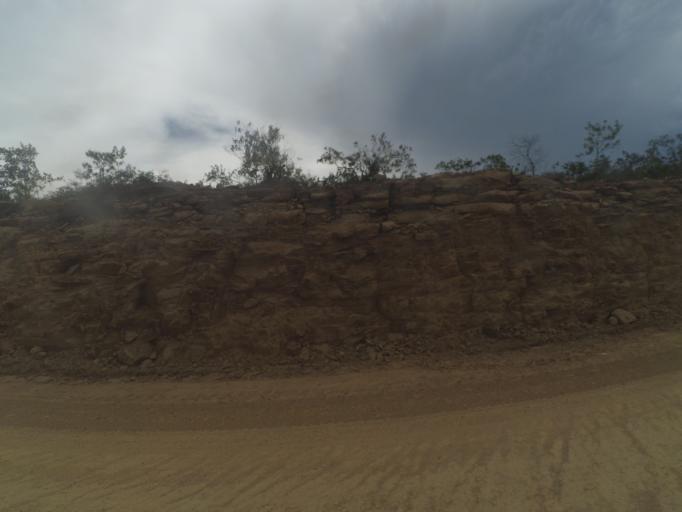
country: BO
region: Chuquisaca
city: Padilla
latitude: -19.3491
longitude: -64.2886
